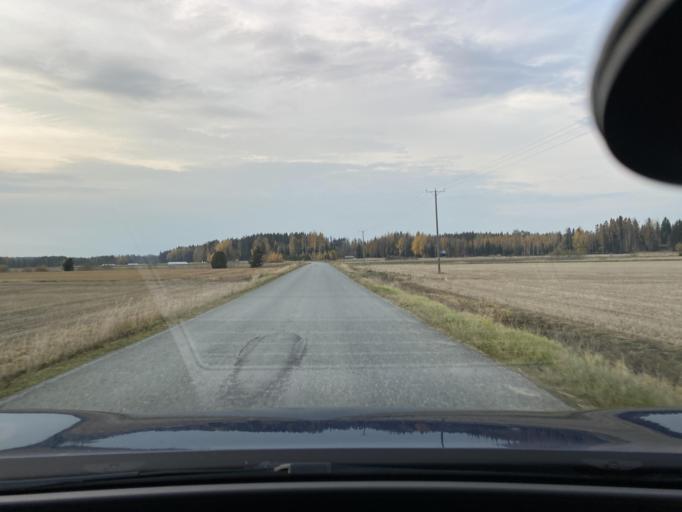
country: FI
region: Pirkanmaa
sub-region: Lounais-Pirkanmaa
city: Punkalaidun
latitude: 61.0778
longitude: 22.9592
